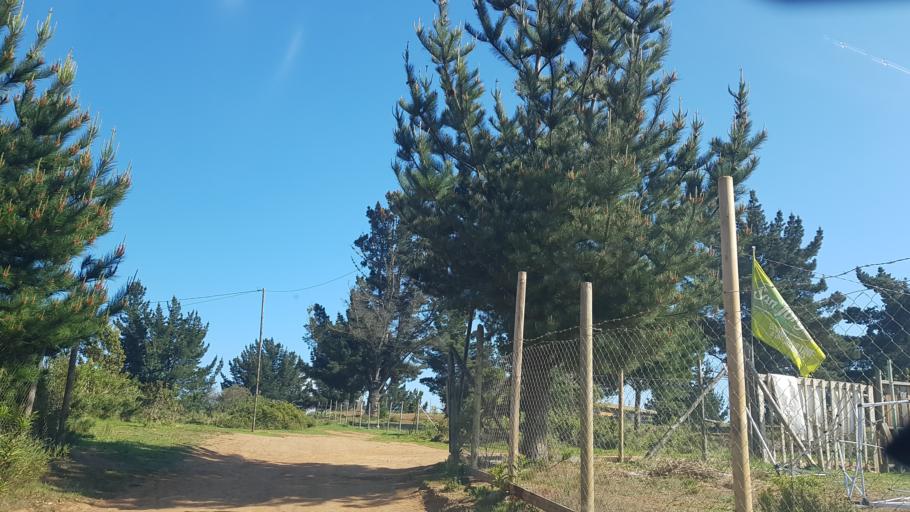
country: CL
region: Valparaiso
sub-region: Provincia de Valparaiso
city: Valparaiso
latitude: -33.1376
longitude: -71.6585
